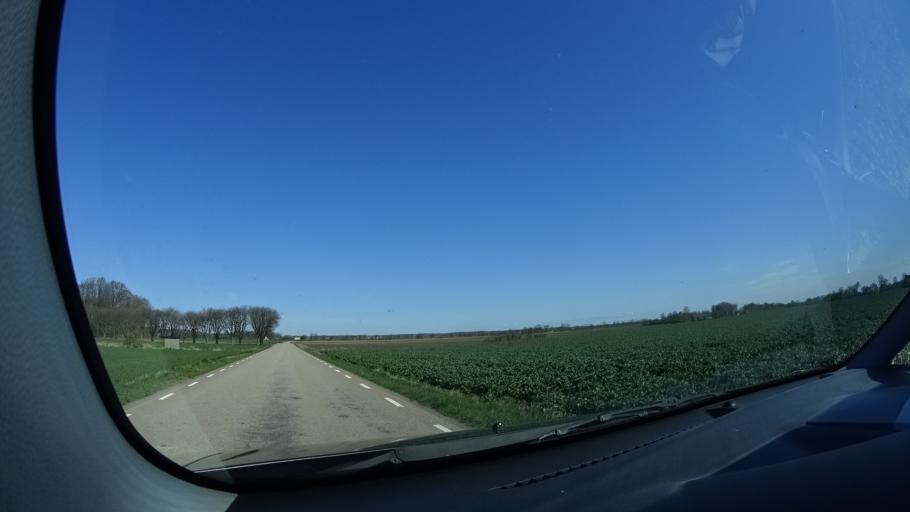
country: SE
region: Skane
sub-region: Hoganas Kommun
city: Hoganas
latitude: 56.2129
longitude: 12.5944
